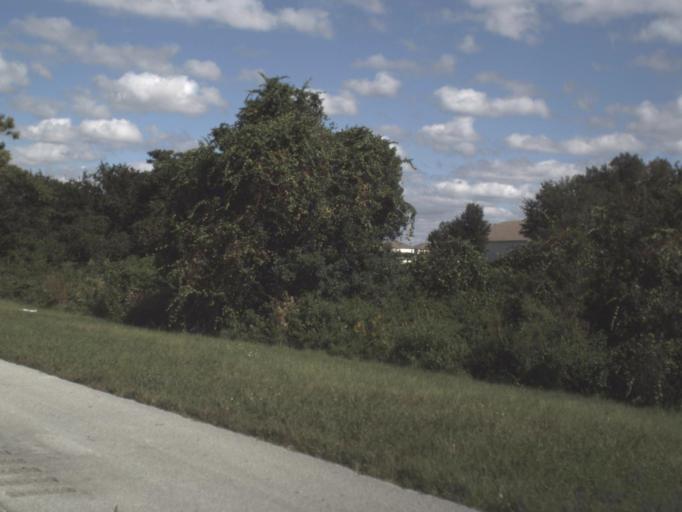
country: US
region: Florida
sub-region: Osceola County
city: Saint Cloud
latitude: 28.2758
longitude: -81.3355
